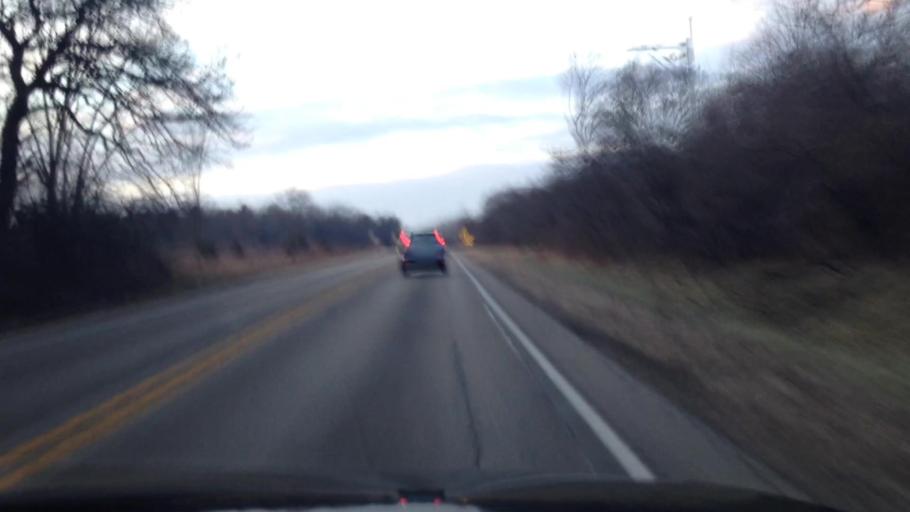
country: US
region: Illinois
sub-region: Kane County
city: Carpentersville
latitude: 42.1278
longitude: -88.2198
